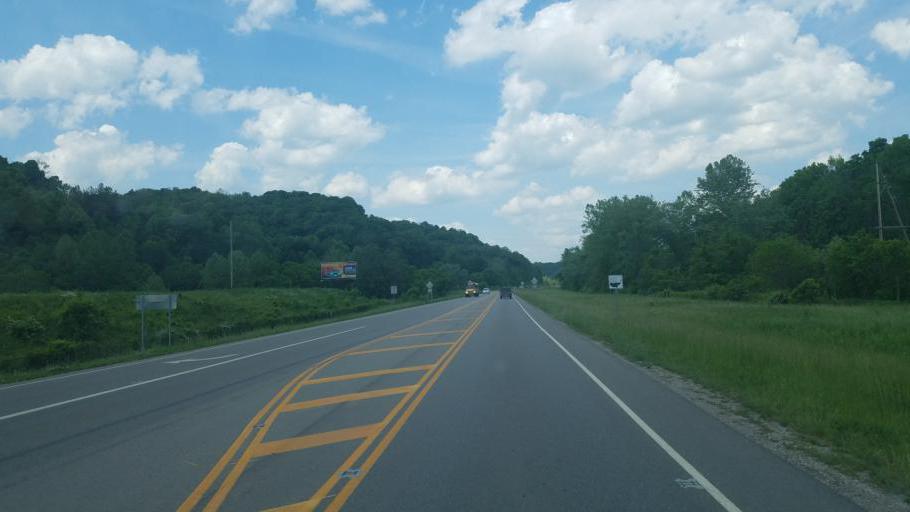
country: US
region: Ohio
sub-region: Meigs County
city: Middleport
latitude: 39.0250
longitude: -82.0663
